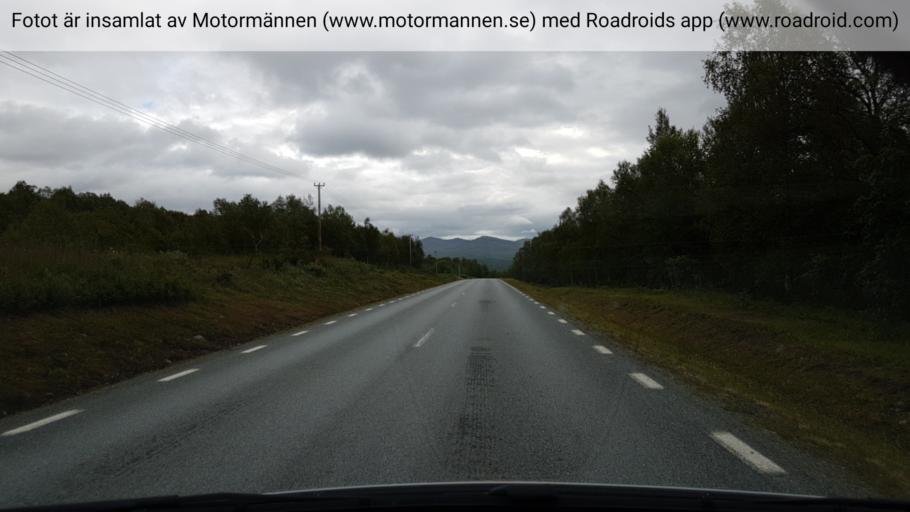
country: NO
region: Nordland
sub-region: Rana
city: Mo i Rana
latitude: 66.0393
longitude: 15.0257
